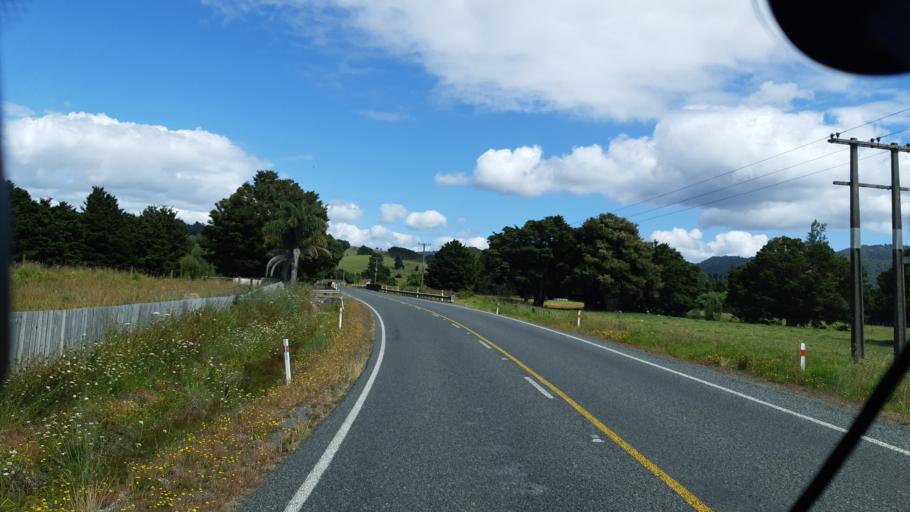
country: NZ
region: Northland
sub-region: Far North District
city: Waimate North
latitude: -35.3038
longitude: 173.7455
